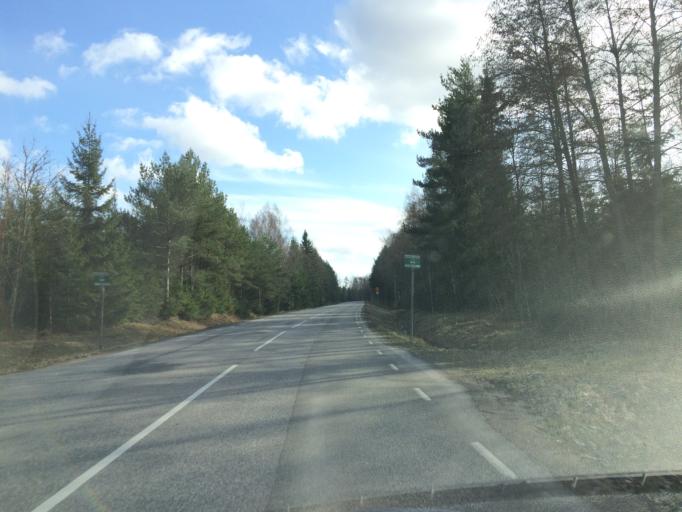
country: SE
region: Kronoberg
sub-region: Almhults Kommun
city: AElmhult
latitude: 56.5926
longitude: 14.0979
